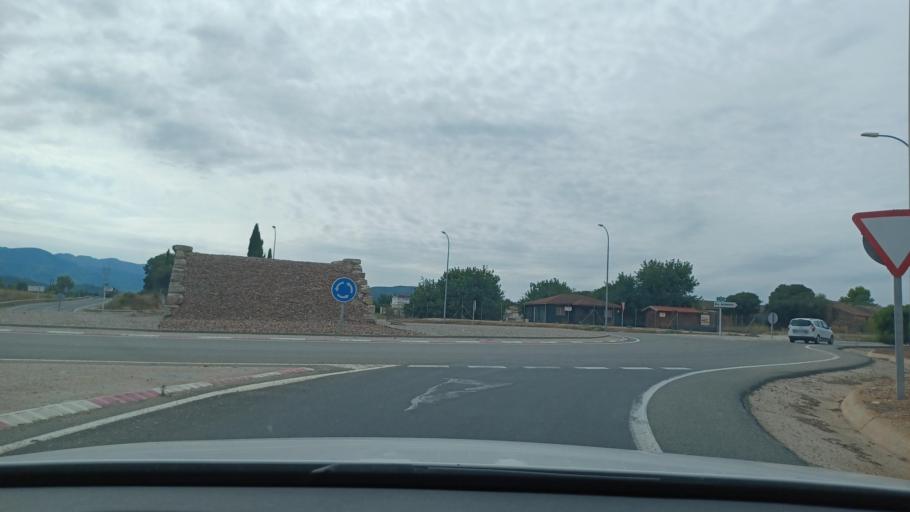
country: ES
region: Catalonia
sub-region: Provincia de Tarragona
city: Santa Barbara
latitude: 40.7172
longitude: 0.5055
